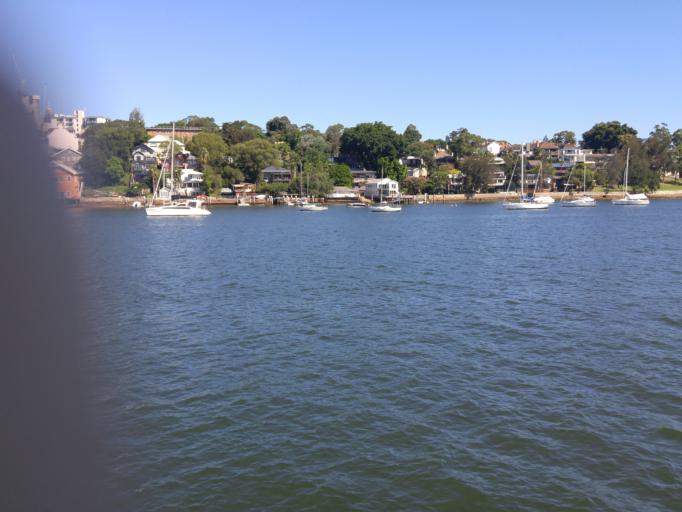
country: AU
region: New South Wales
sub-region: Leichhardt
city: Balmain East
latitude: -33.8533
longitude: 151.1902
